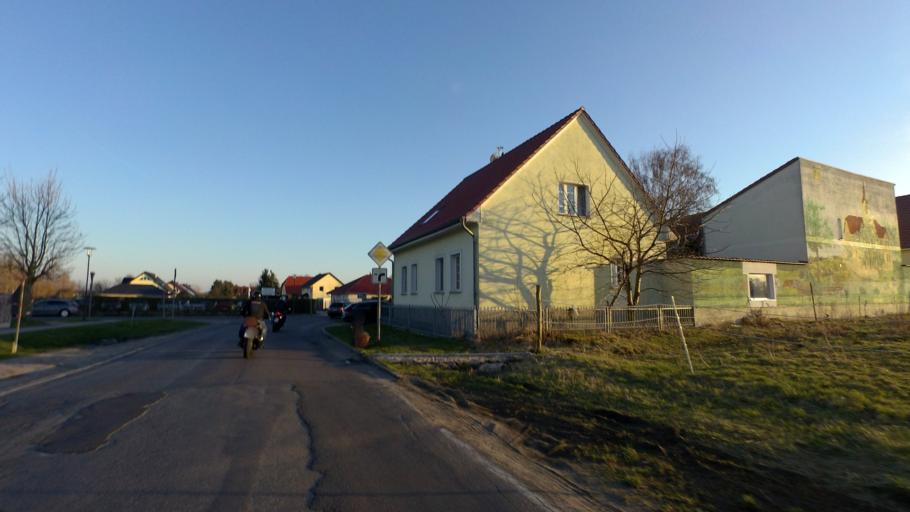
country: DE
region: Berlin
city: Hellersdorf
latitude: 52.5510
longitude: 13.6365
